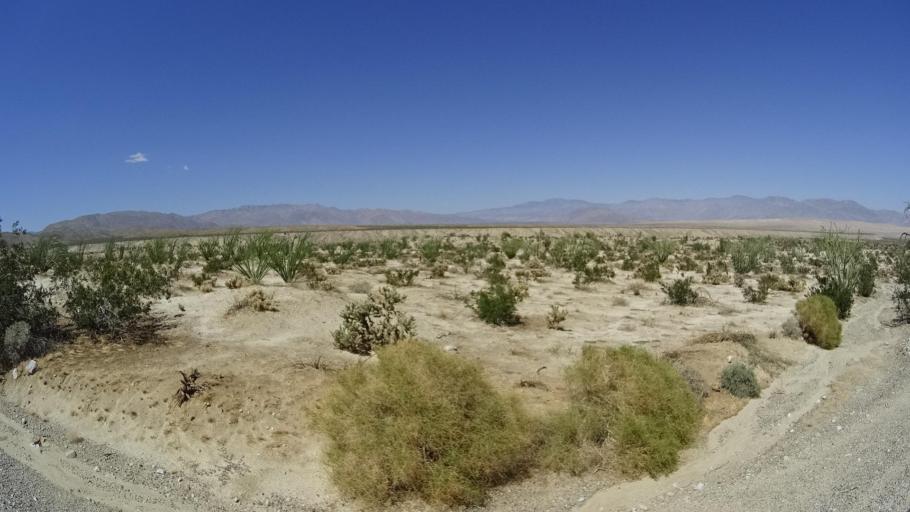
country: US
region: California
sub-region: San Diego County
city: Borrego Springs
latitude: 33.1435
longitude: -116.2684
